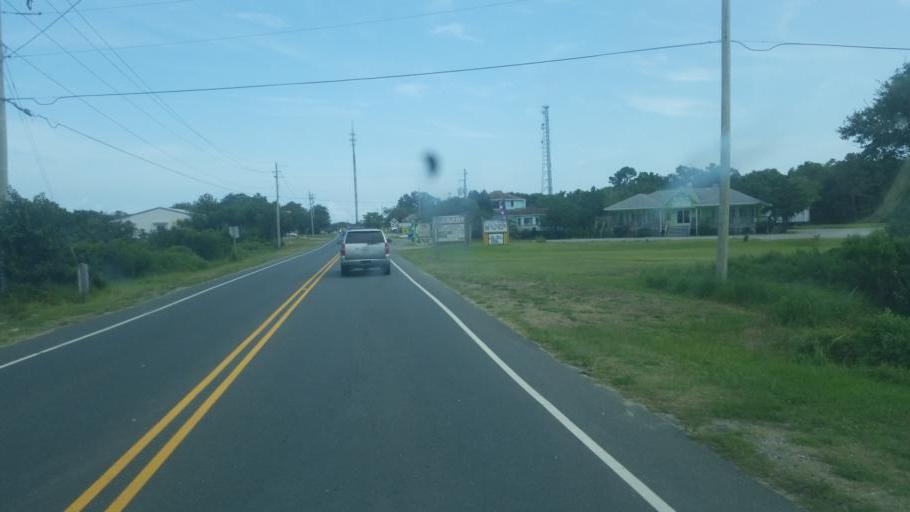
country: US
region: North Carolina
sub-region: Dare County
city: Buxton
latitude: 35.2674
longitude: -75.5318
